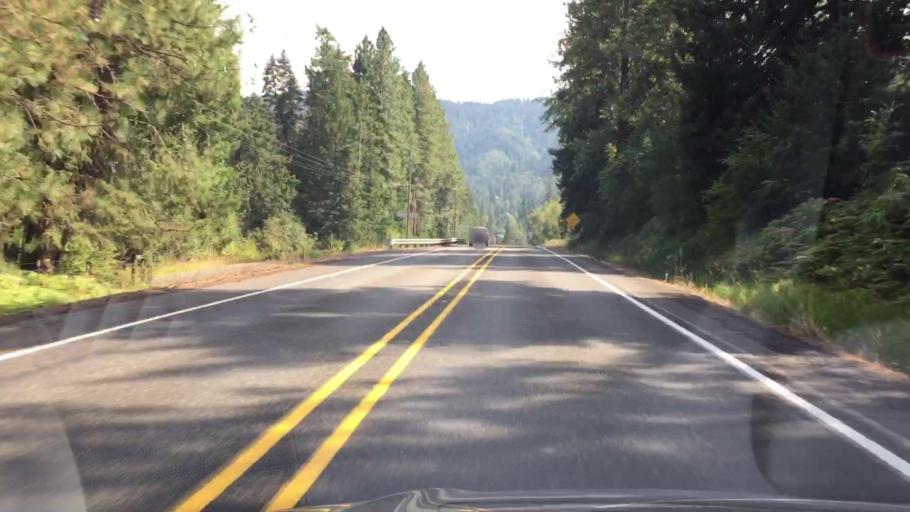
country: US
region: Washington
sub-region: Klickitat County
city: White Salmon
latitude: 45.8039
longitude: -121.4891
